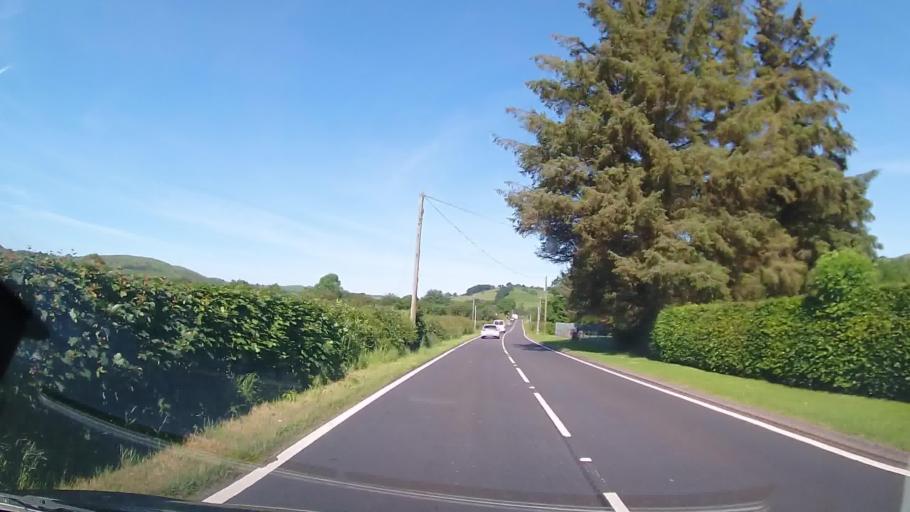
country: GB
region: Wales
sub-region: Sir Powys
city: Llangynog
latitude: 52.6914
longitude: -3.4722
